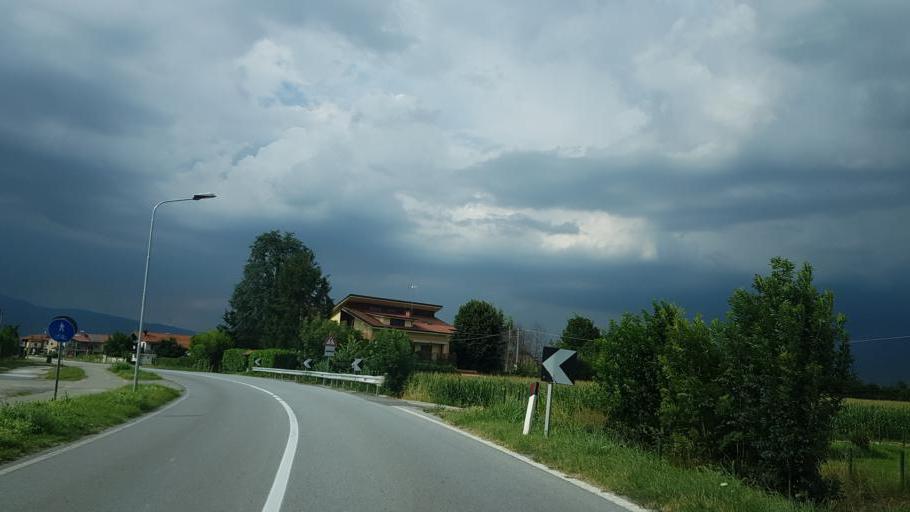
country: IT
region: Piedmont
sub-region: Provincia di Cuneo
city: Cervasca
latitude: 44.3746
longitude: 7.4760
